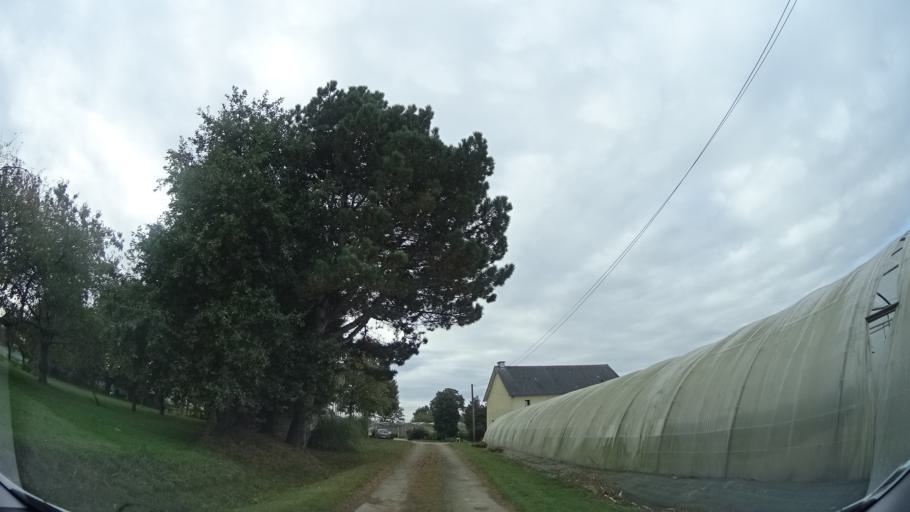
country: FR
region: Brittany
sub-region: Departement d'Ille-et-Vilaine
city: Vignoc
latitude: 48.2357
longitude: -1.7790
